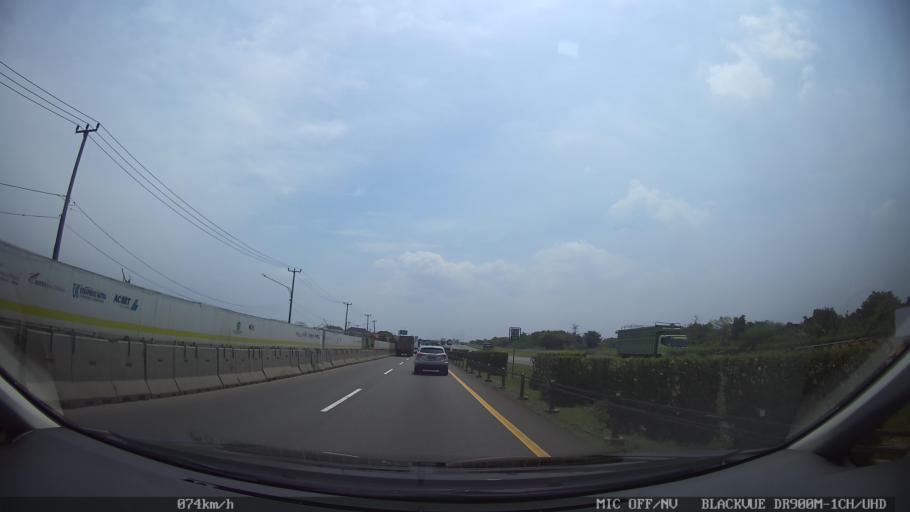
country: ID
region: Banten
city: Serang
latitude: -6.1389
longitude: 106.2557
